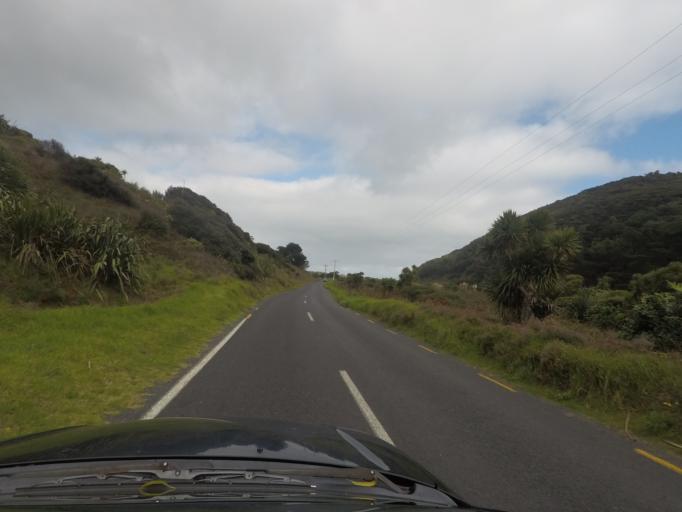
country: NZ
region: Auckland
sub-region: Auckland
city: Muriwai Beach
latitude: -36.8861
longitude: 174.4513
